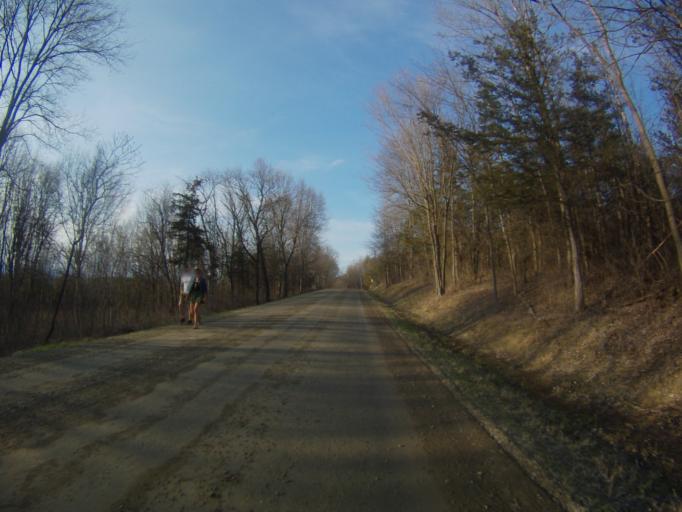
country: US
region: Vermont
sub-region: Addison County
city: Vergennes
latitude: 44.0483
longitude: -73.2920
